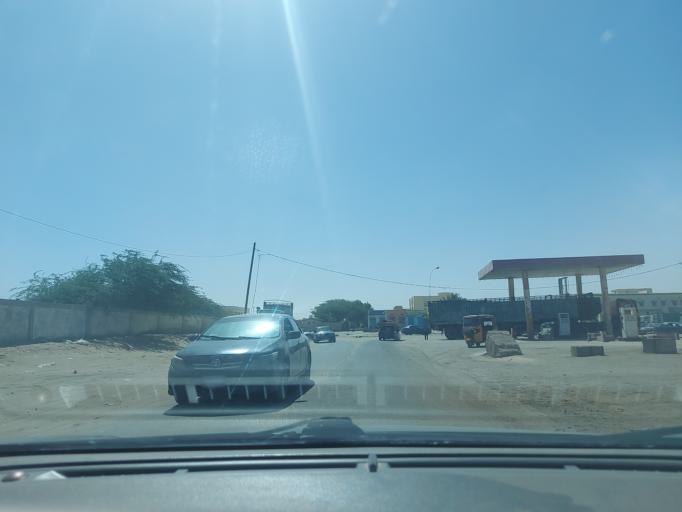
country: MR
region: Nouakchott
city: Nouakchott
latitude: 18.0609
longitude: -15.9741
